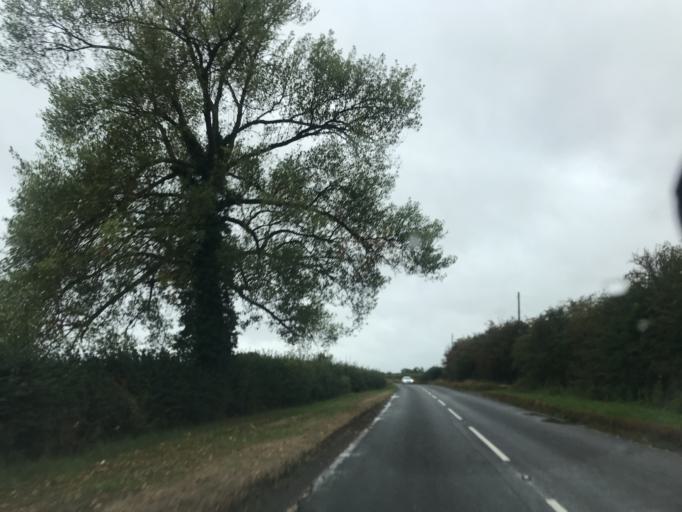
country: GB
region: England
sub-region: Buckinghamshire
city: Stone
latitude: 51.7920
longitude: -0.8645
